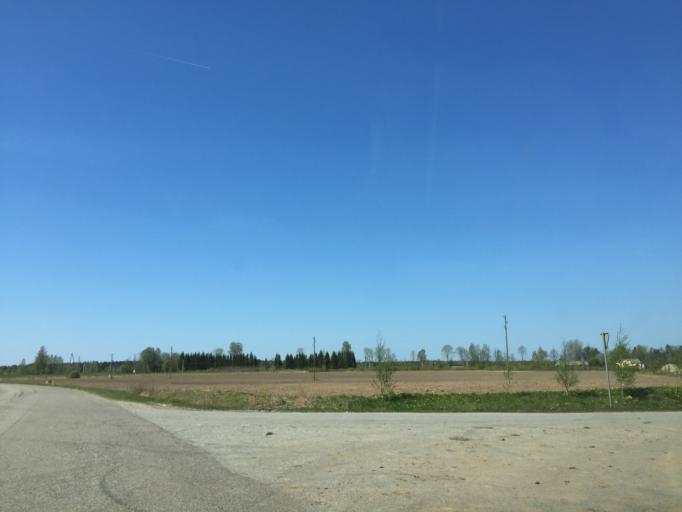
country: LV
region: Saulkrastu
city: Saulkrasti
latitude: 57.3298
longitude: 24.4664
